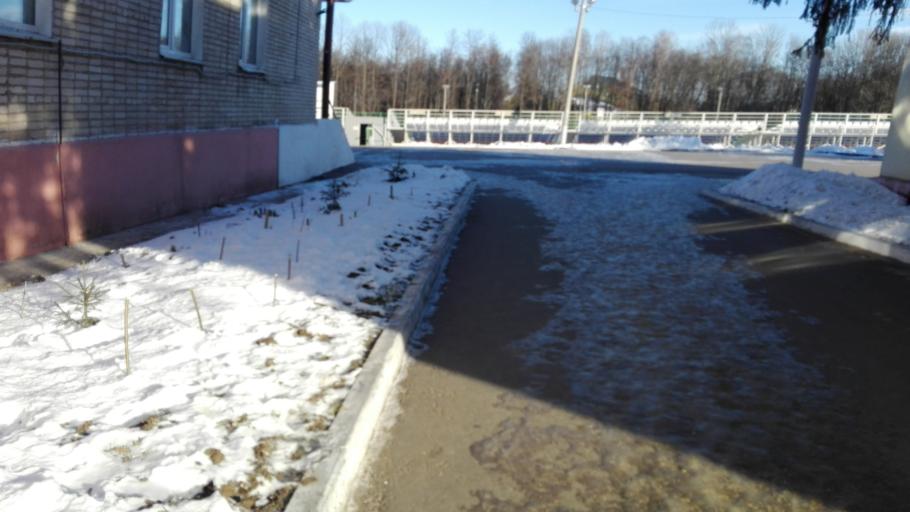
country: RU
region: Tula
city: Kosaya Gora
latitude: 54.1203
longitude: 37.5397
